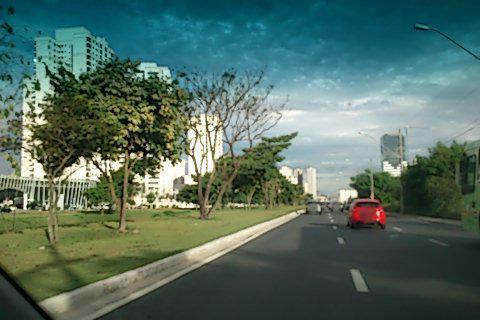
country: BR
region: Sao Paulo
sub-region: Sao Jose Dos Campos
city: Sao Jose dos Campos
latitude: -23.1999
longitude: -45.9122
